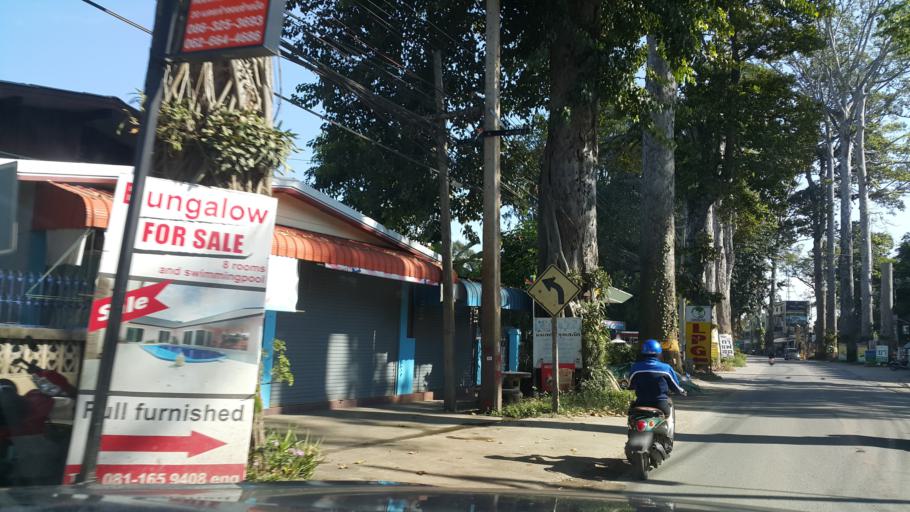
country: TH
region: Chiang Mai
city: Saraphi
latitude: 18.7357
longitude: 99.0162
